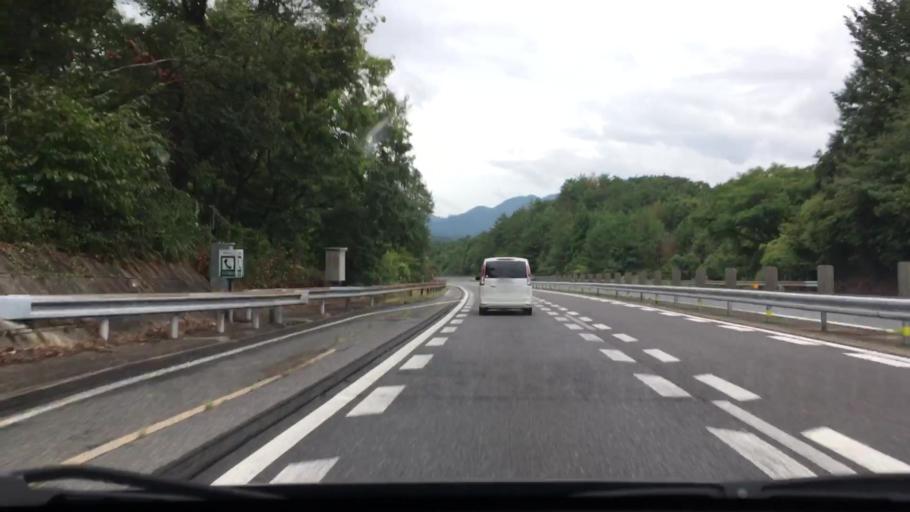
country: JP
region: Hiroshima
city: Miyoshi
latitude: 34.6895
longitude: 132.5666
